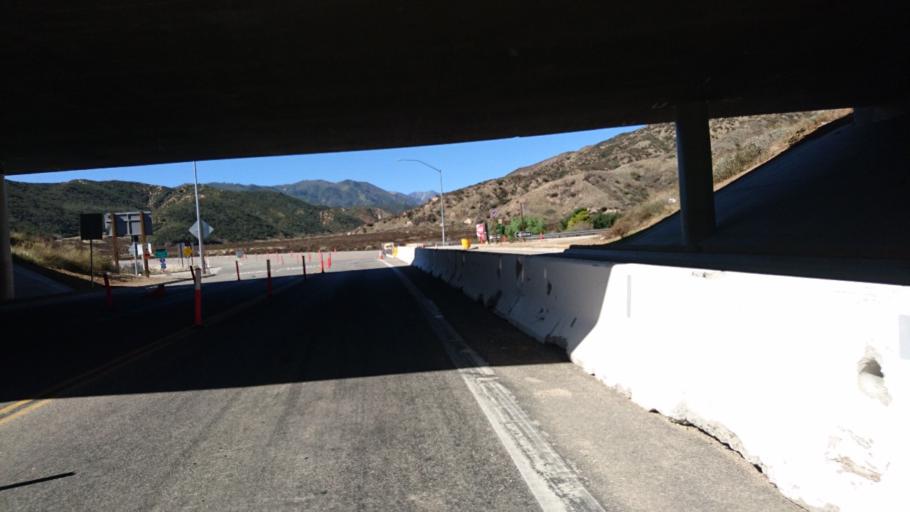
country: US
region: California
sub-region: San Bernardino County
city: Muscoy
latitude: 34.2027
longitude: -117.4154
